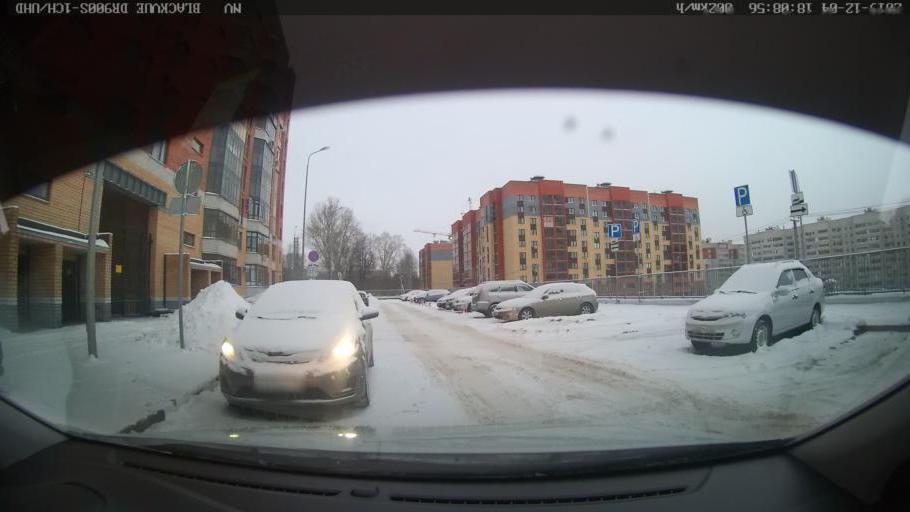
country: RU
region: Tatarstan
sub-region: Gorod Kazan'
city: Kazan
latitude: 55.8024
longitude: 49.2021
